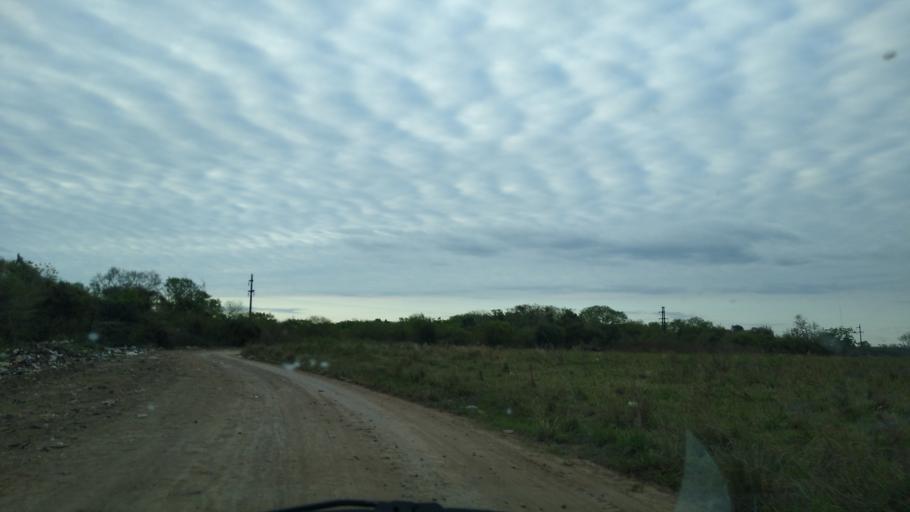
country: AR
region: Chaco
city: Fontana
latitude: -27.3921
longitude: -59.0503
